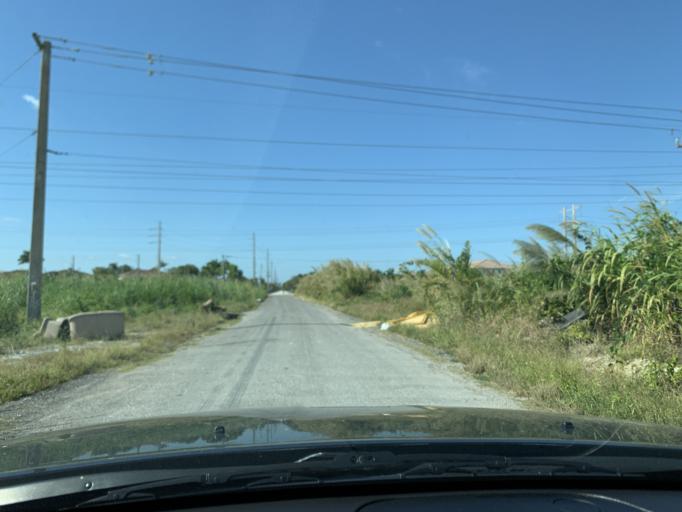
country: US
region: Florida
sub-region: Miami-Dade County
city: Three Lakes
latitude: 25.6414
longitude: -80.3973
